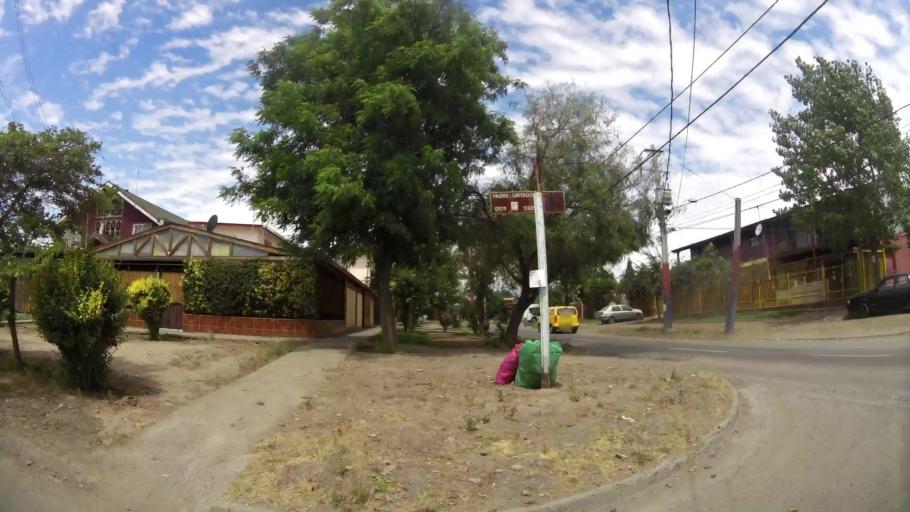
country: CL
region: Santiago Metropolitan
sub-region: Provincia de Santiago
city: La Pintana
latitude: -33.5801
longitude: -70.6533
